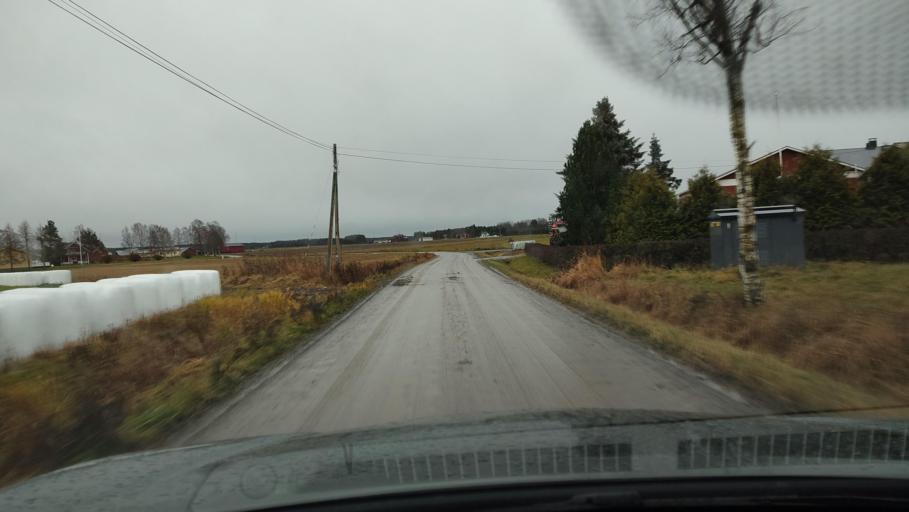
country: FI
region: Southern Ostrobothnia
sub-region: Suupohja
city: Karijoki
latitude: 62.2462
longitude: 21.5486
